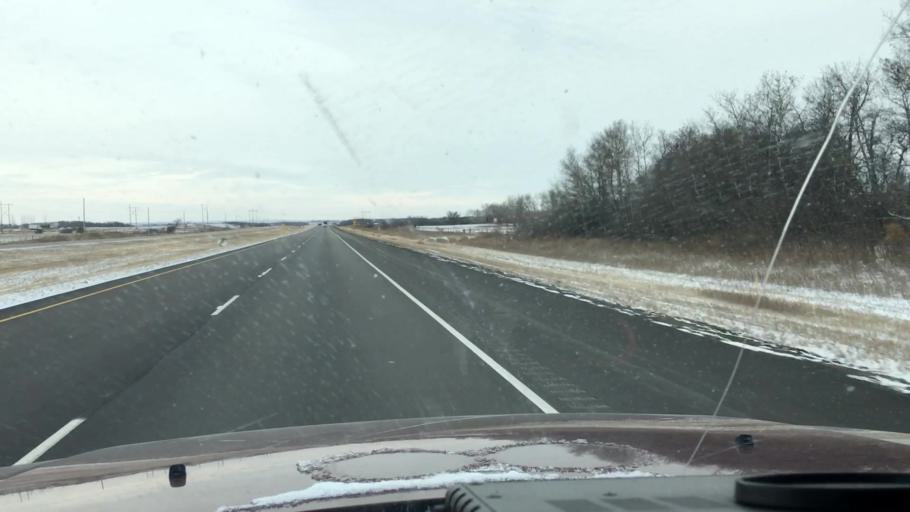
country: CA
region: Saskatchewan
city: Saskatoon
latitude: 51.8996
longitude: -106.5211
